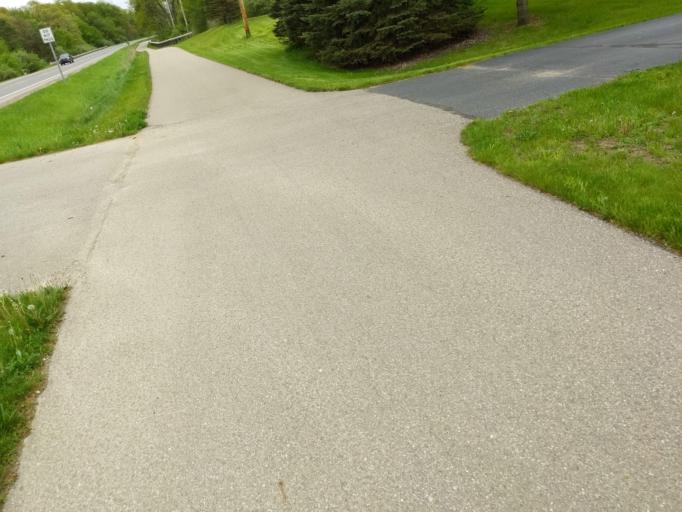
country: US
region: Michigan
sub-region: Washtenaw County
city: Chelsea
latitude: 42.3489
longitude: -84.0471
